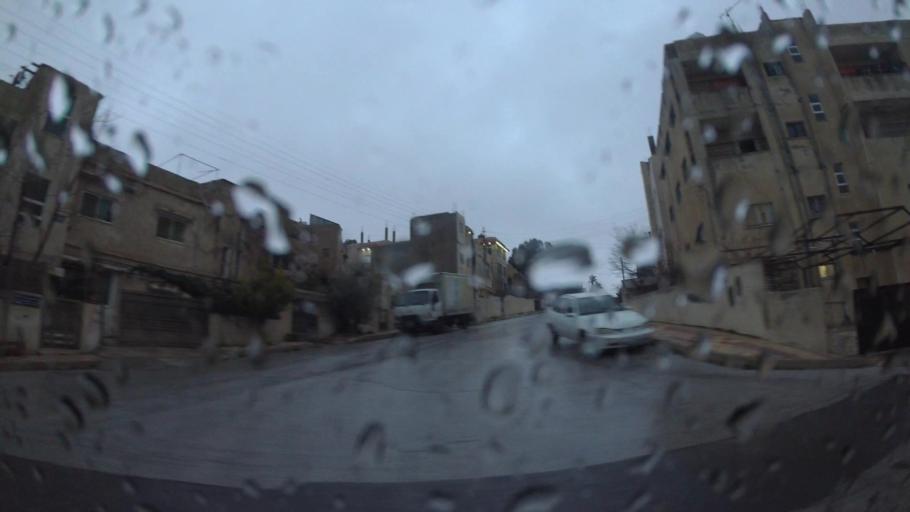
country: JO
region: Amman
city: Al Jubayhah
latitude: 32.0283
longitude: 35.8467
